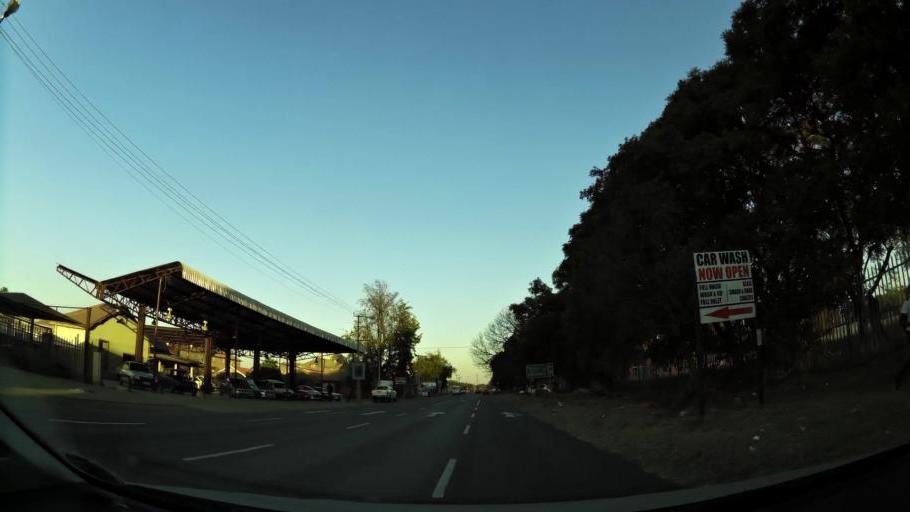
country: ZA
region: North-West
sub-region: Bojanala Platinum District Municipality
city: Rustenburg
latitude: -25.6734
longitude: 27.2495
